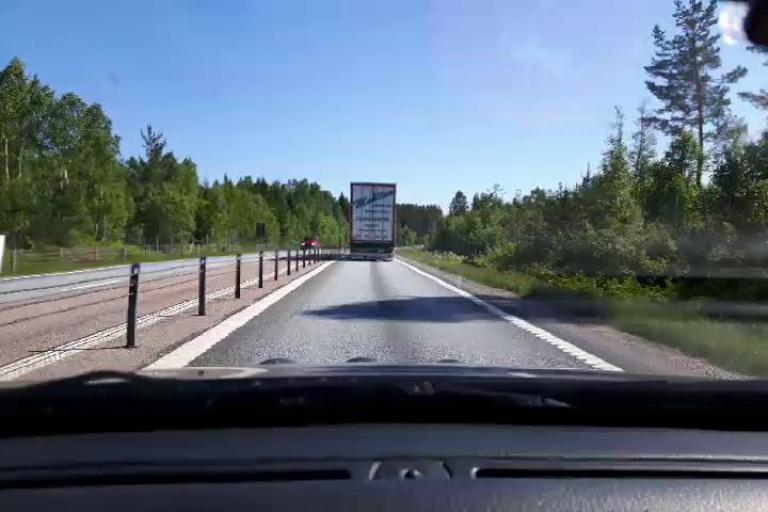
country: SE
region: Gaevleborg
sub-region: Soderhamns Kommun
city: Soderhamn
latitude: 61.2602
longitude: 17.0337
